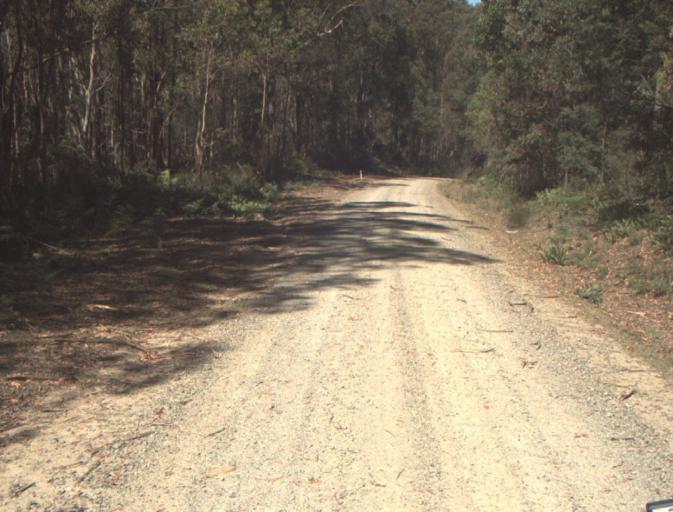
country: AU
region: Tasmania
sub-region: Dorset
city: Scottsdale
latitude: -41.3832
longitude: 147.4987
